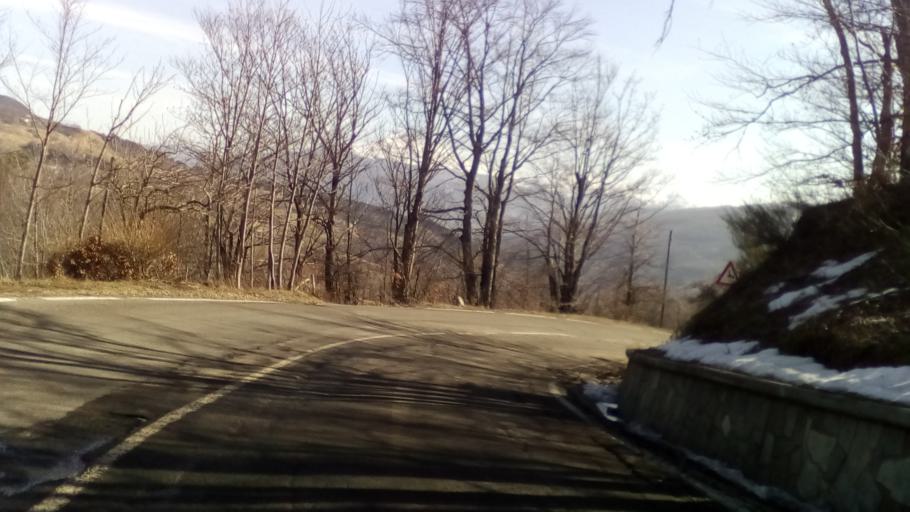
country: IT
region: Emilia-Romagna
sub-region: Provincia di Modena
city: Pievepelago
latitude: 44.1985
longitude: 10.5294
